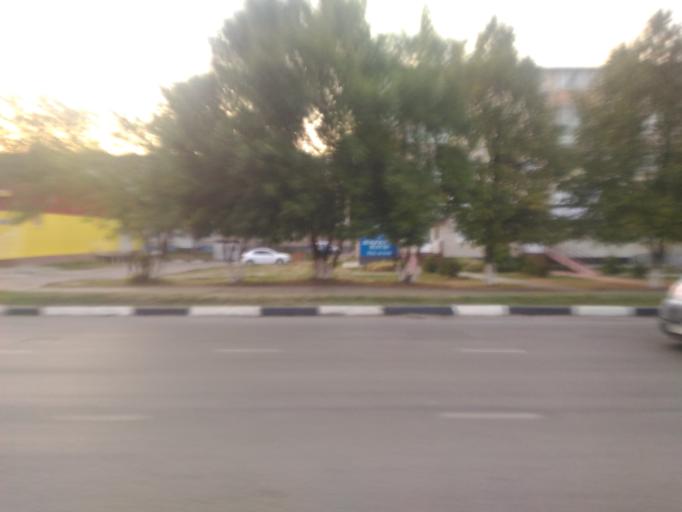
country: RU
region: Ulyanovsk
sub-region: Ulyanovskiy Rayon
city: Ulyanovsk
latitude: 54.2789
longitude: 48.2943
